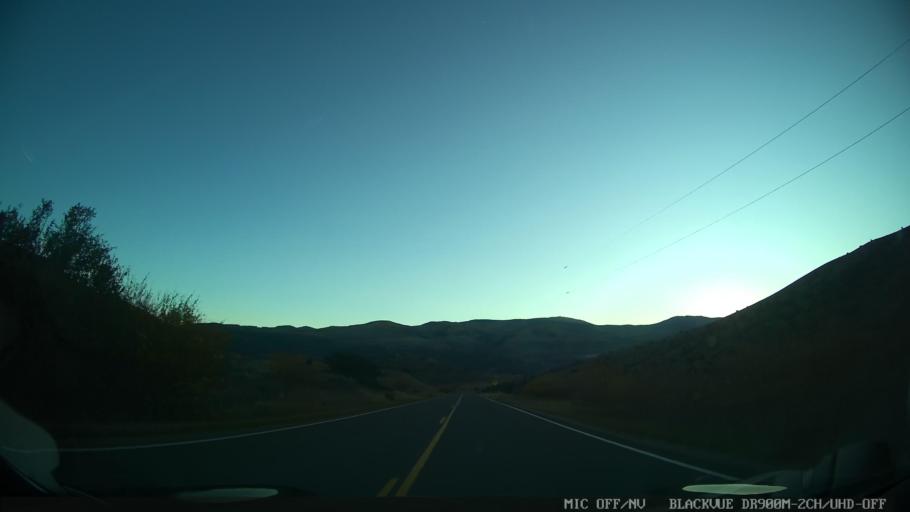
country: US
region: Colorado
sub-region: Eagle County
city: Edwards
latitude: 39.8210
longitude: -106.6475
